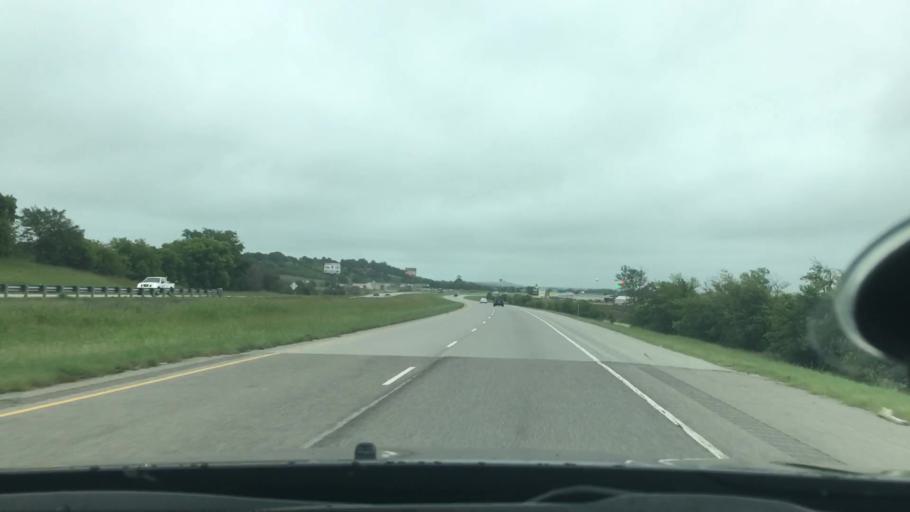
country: US
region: Oklahoma
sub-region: Okfuskee County
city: Okemah
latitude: 35.4176
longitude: -96.3167
